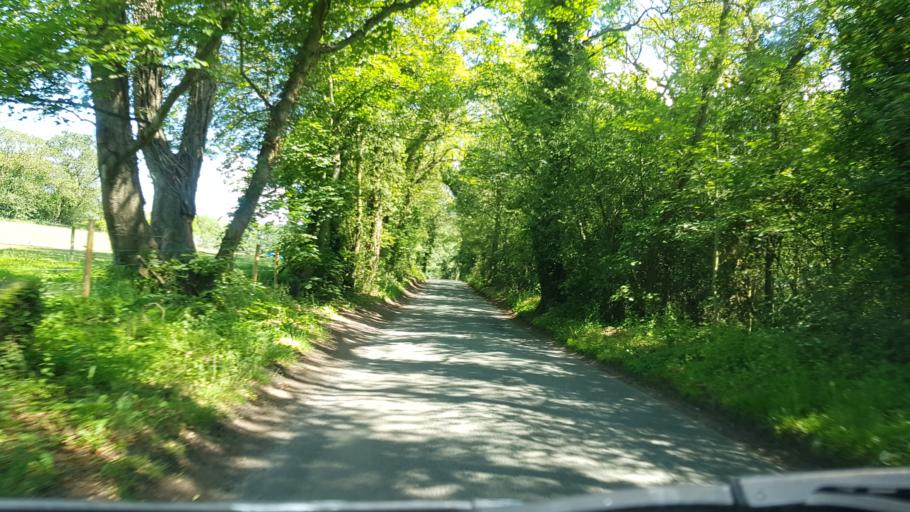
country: GB
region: England
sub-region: Worcestershire
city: Kidderminster
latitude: 52.4409
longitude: -2.2586
